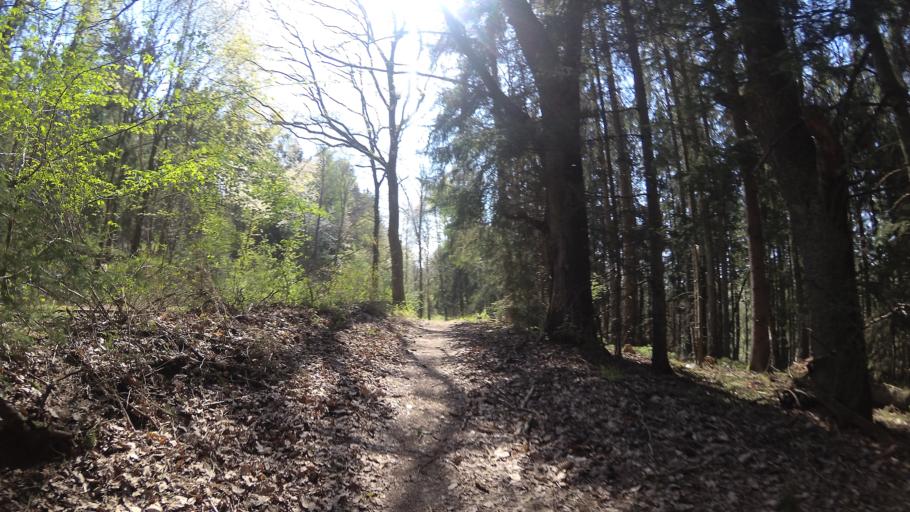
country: DE
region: Saarland
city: Ottweiler
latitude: 49.4146
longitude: 7.1892
